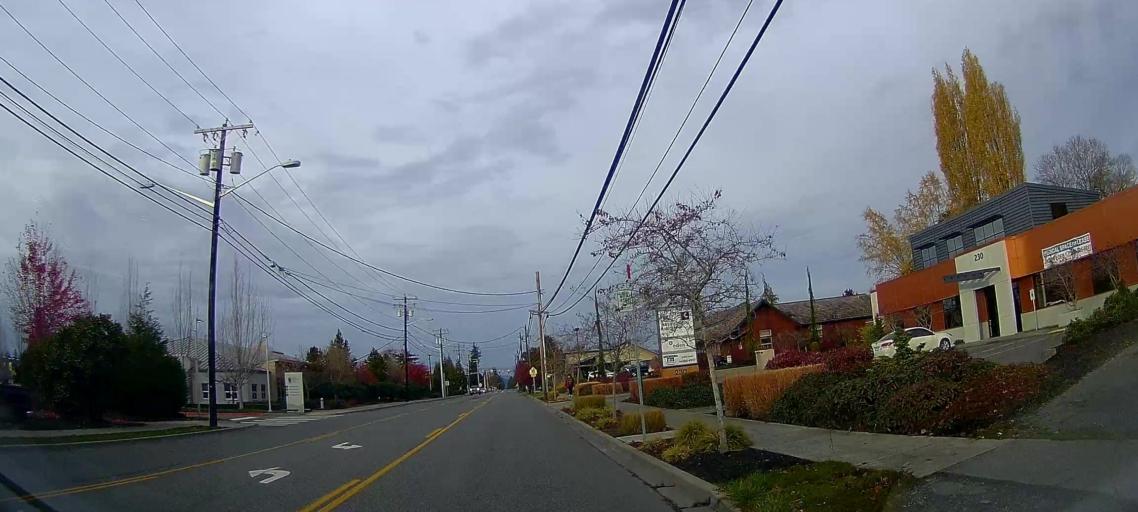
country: US
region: Washington
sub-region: Skagit County
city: Mount Vernon
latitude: 48.4191
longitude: -122.3229
